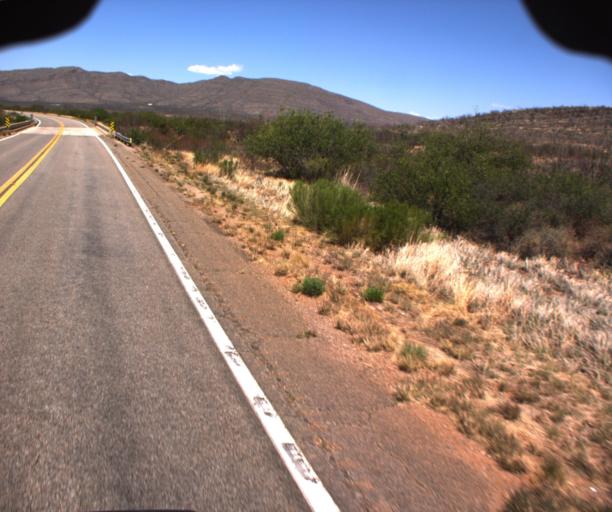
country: US
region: Arizona
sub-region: Cochise County
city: Bisbee
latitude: 31.5476
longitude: -110.0112
